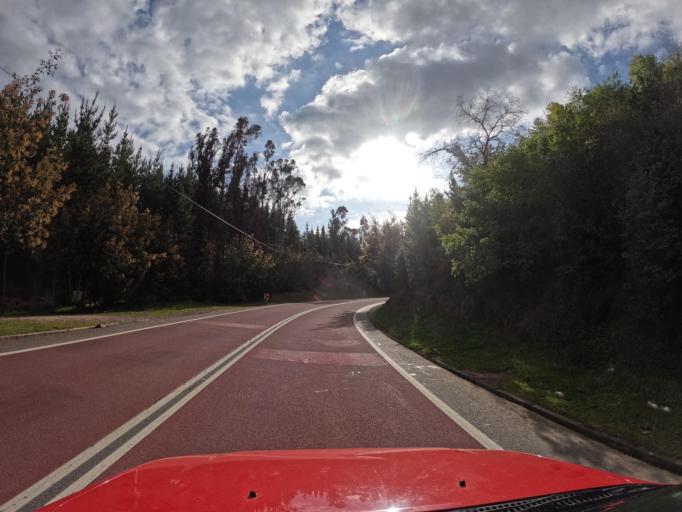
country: CL
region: Maule
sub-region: Provincia de Talca
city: Constitucion
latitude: -35.5504
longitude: -72.1453
